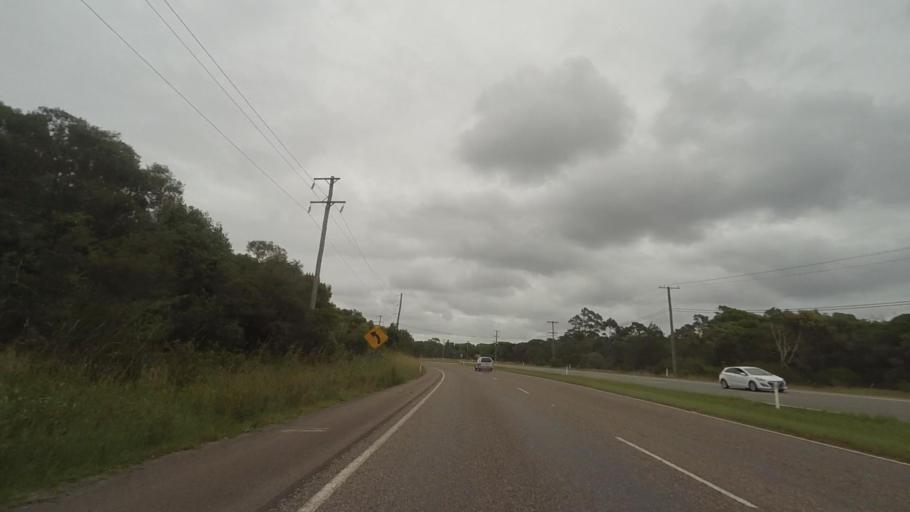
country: AU
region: New South Wales
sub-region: Wyong Shire
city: Kingfisher Shores
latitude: -33.1890
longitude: 151.5296
